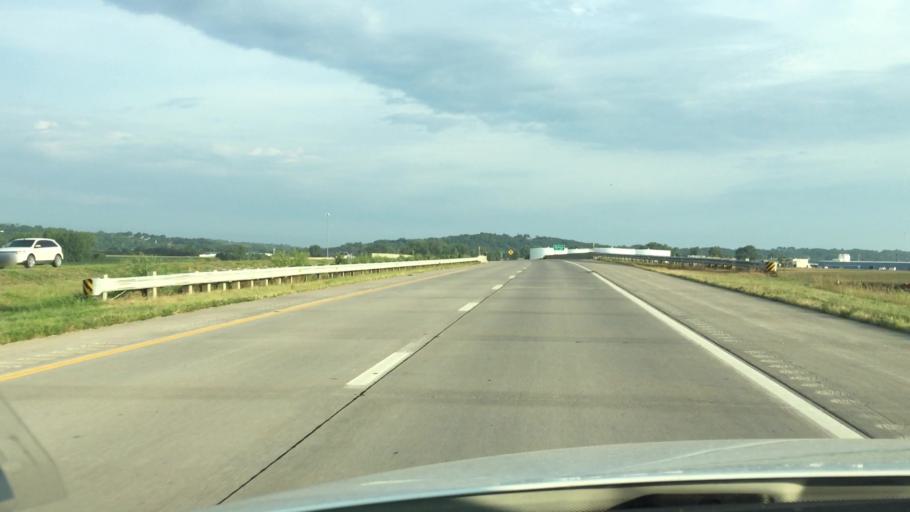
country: US
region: Kansas
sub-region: Doniphan County
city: Wathena
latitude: 39.7463
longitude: -94.9237
